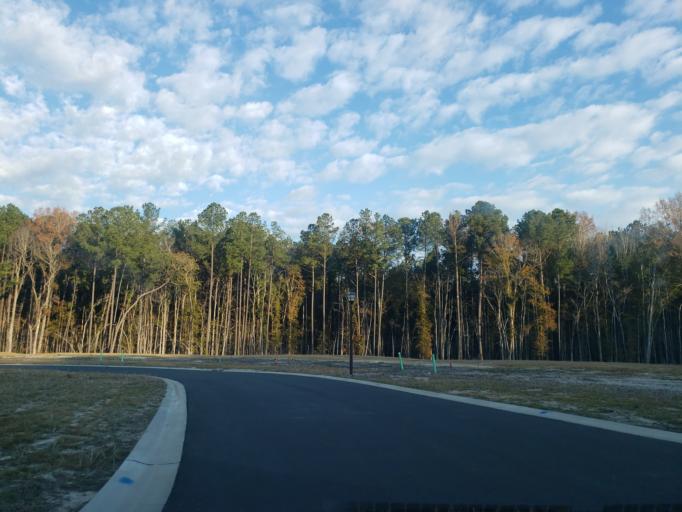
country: US
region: Georgia
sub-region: Chatham County
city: Pooler
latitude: 32.1565
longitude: -81.2597
